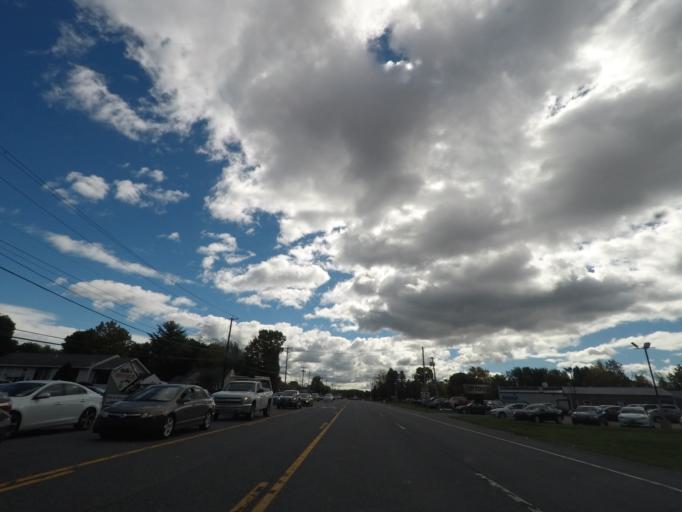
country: US
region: New York
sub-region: Saratoga County
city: Waterford
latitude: 42.8404
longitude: -73.7448
